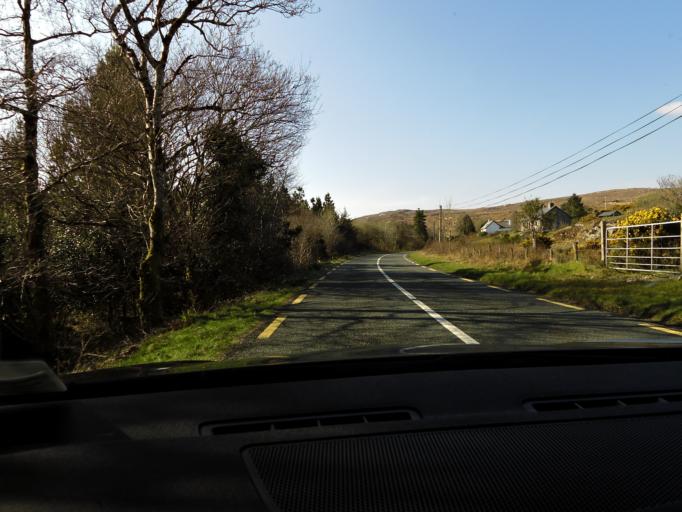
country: IE
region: Connaught
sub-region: County Galway
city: Clifden
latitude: 53.4746
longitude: -9.8835
